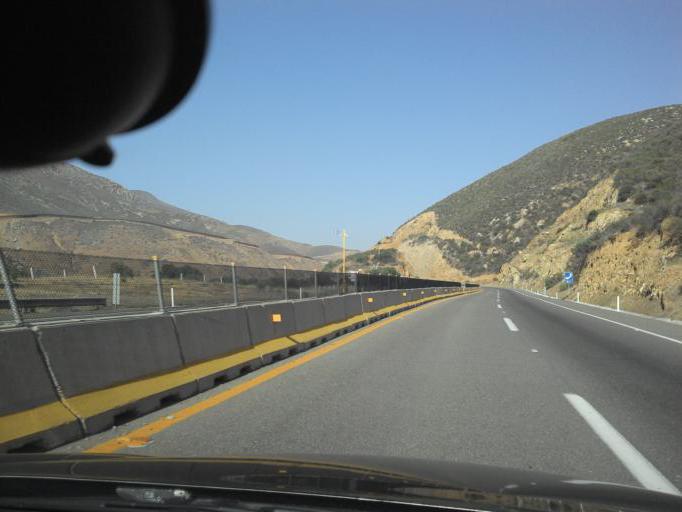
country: MX
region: Baja California
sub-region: Tijuana
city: El Nino
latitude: 32.5563
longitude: -116.8268
